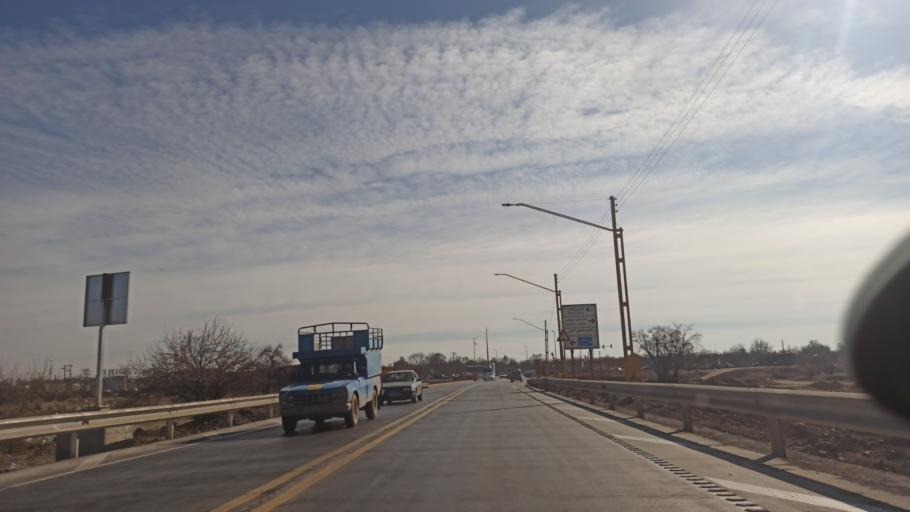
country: IR
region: Qazvin
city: Qazvin
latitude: 36.2575
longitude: 49.9777
